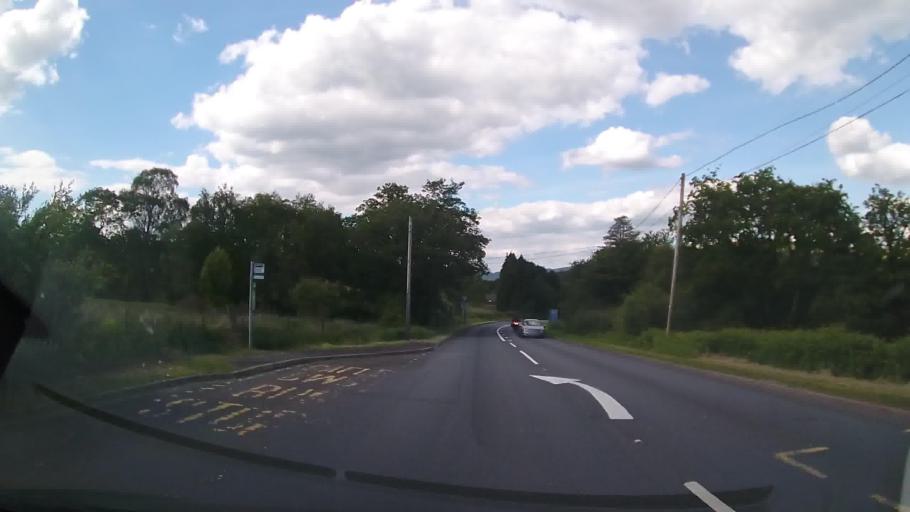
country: GB
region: Wales
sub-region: Gwynedd
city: Dolgellau
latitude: 52.7325
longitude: -3.8286
